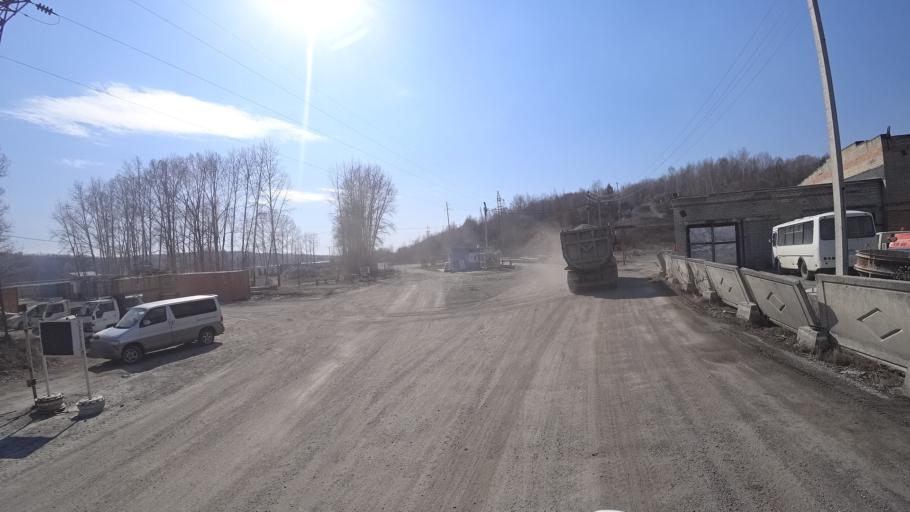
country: RU
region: Amur
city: Novobureyskiy
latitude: 49.7901
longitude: 129.9610
